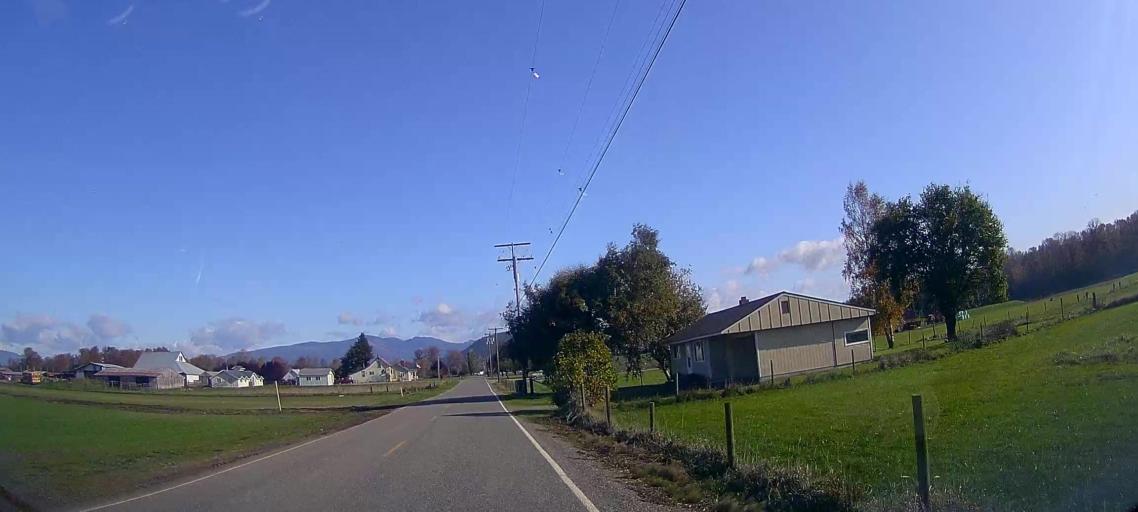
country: US
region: Washington
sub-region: Skagit County
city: Mount Vernon
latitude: 48.3991
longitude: -122.3767
